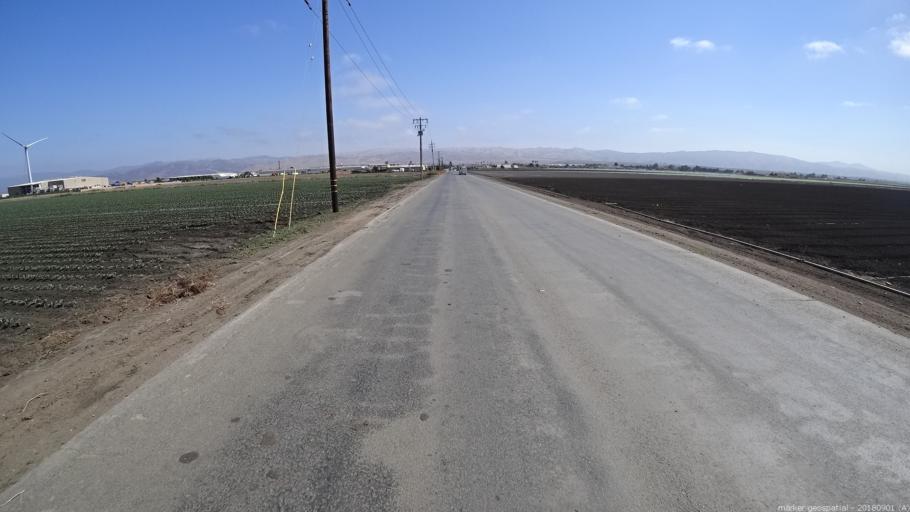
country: US
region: California
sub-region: Monterey County
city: Gonzales
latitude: 36.4977
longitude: -121.4508
